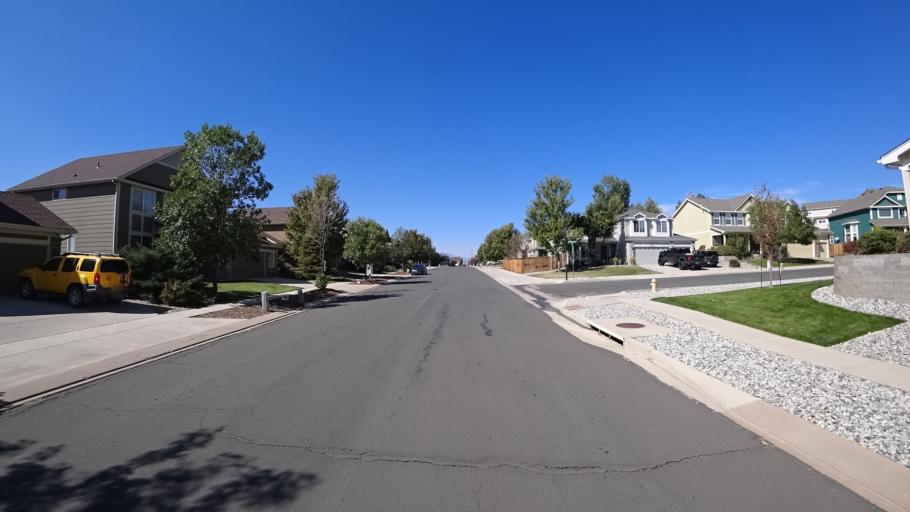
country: US
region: Colorado
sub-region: El Paso County
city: Cimarron Hills
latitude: 38.8988
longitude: -104.6929
